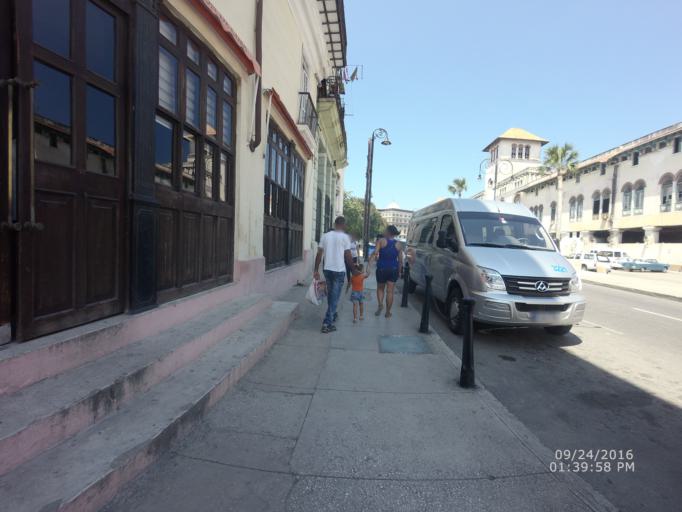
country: CU
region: La Habana
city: La Habana Vieja
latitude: 23.1355
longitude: -82.3480
